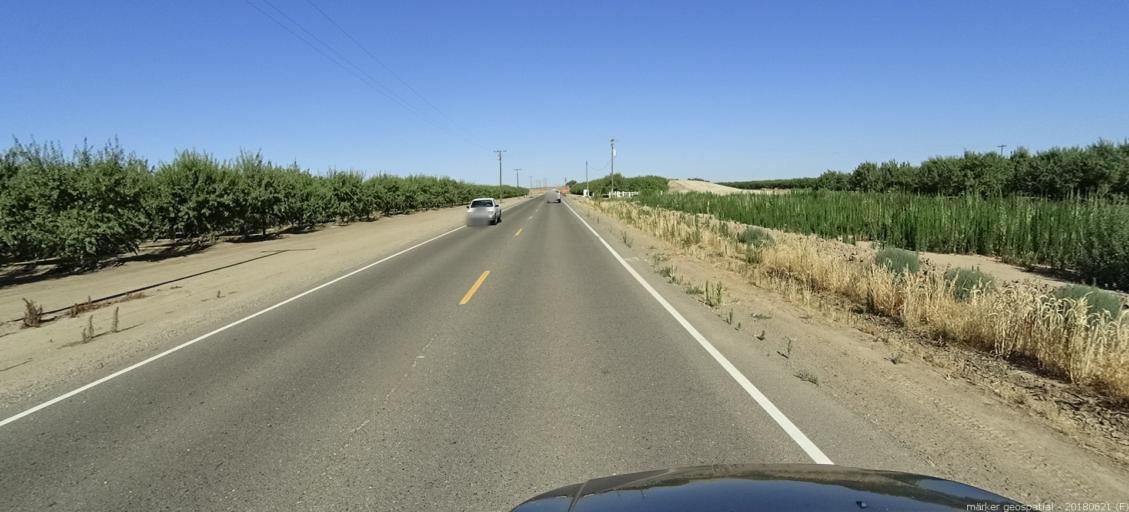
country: US
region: California
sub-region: Fresno County
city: Biola
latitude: 36.8513
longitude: -119.9366
